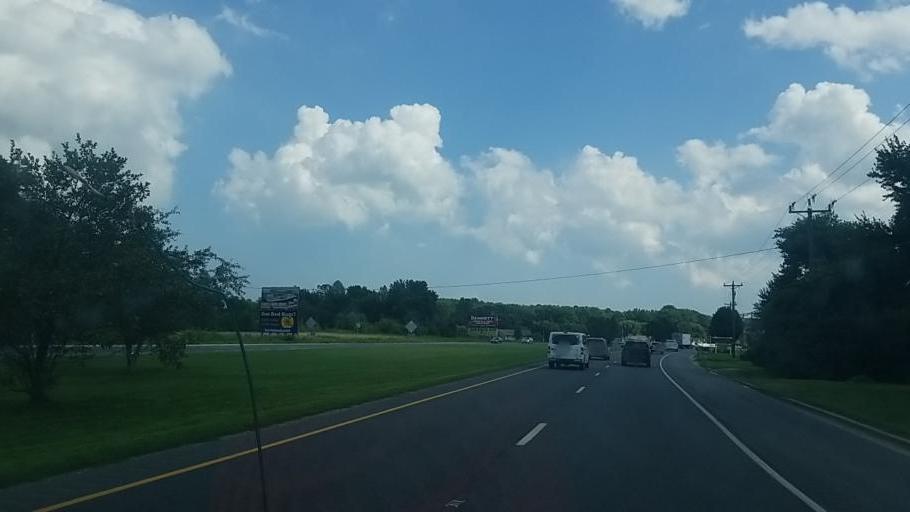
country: US
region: Delaware
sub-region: Sussex County
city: Selbyville
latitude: 38.5173
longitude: -75.2402
